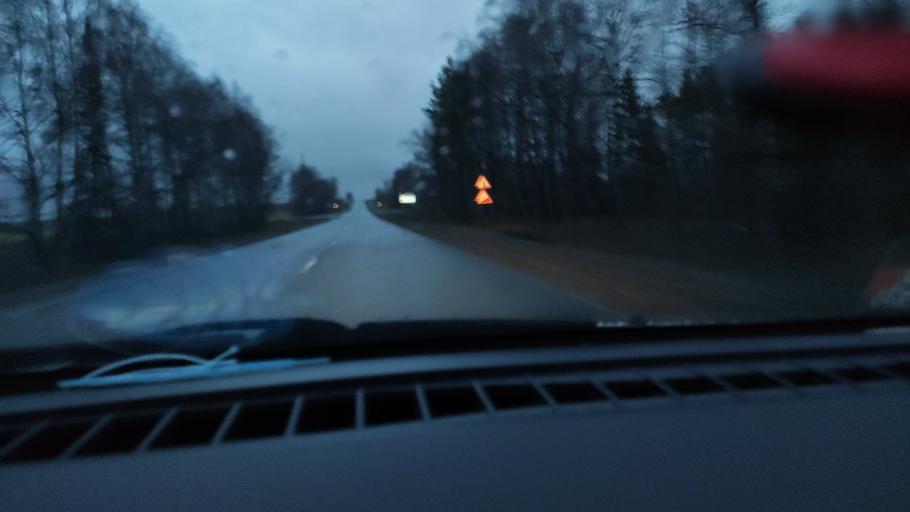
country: RU
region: Udmurtiya
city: Mozhga
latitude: 56.3075
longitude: 52.3374
